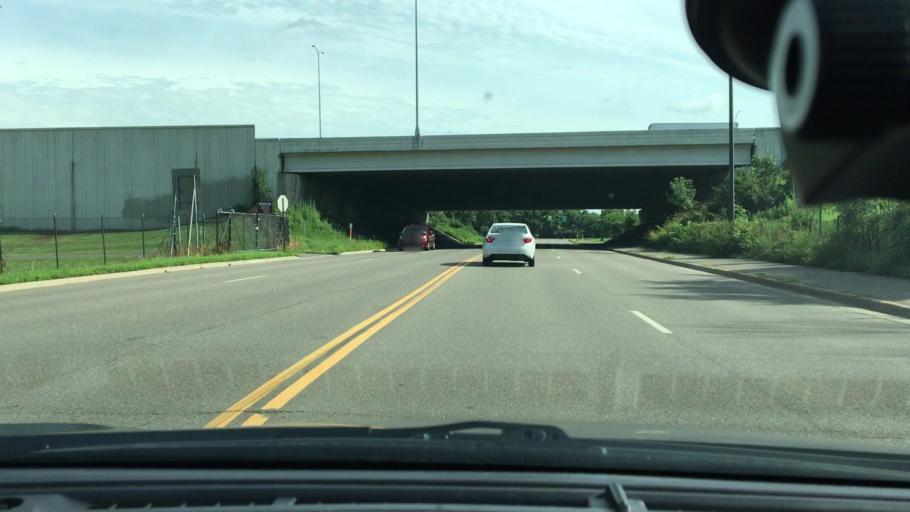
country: US
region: Minnesota
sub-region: Hennepin County
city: Saint Louis Park
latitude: 44.9749
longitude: -93.3909
